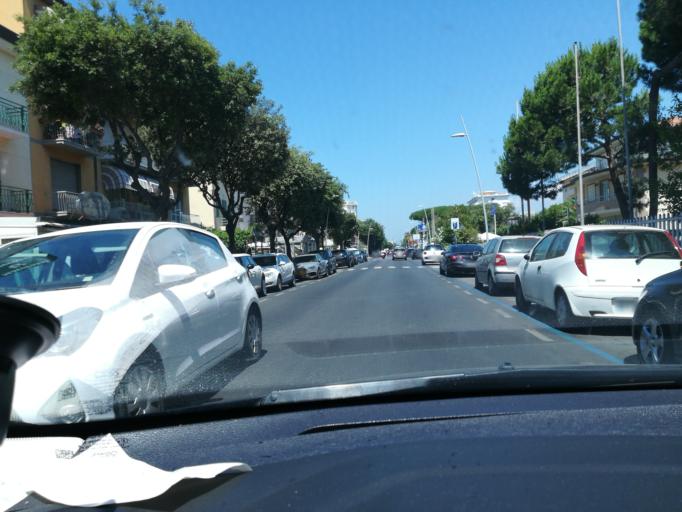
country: IT
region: Tuscany
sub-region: Provincia di Lucca
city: Camaiore
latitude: 43.8954
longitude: 10.2252
